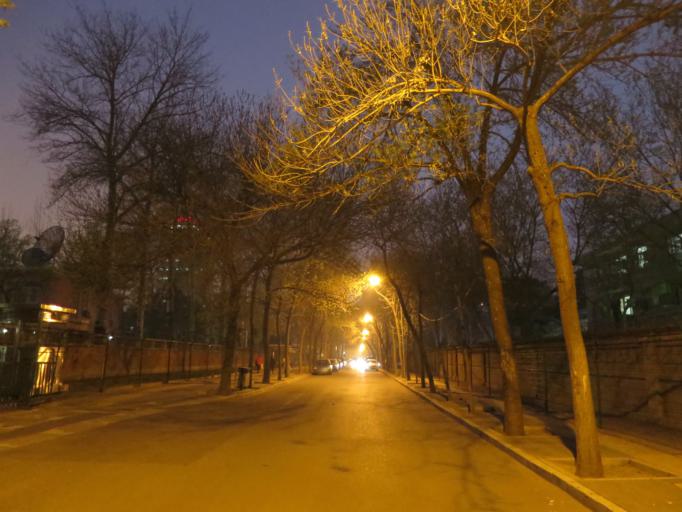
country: CN
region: Beijing
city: Chaowai
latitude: 39.9090
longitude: 116.4397
